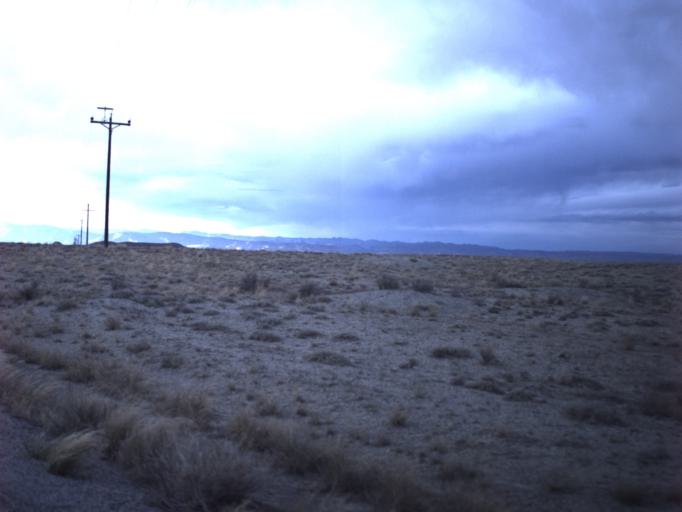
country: US
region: Utah
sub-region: Grand County
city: Moab
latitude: 38.9025
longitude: -109.3165
